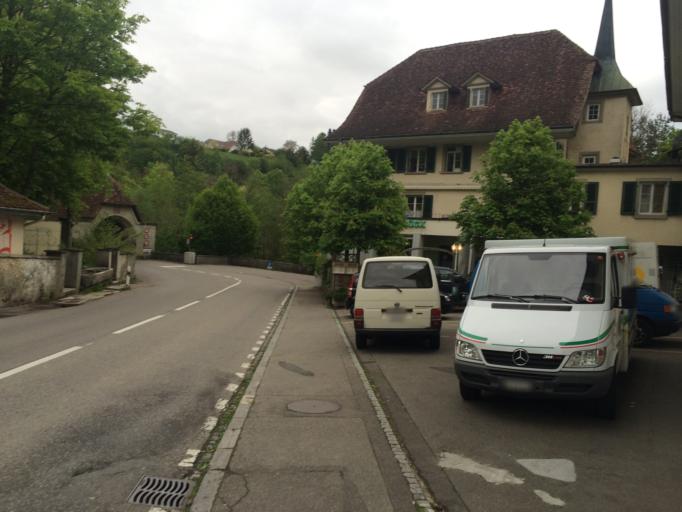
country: CH
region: Bern
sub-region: Bern-Mittelland District
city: Kirchlindach
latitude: 46.9730
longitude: 7.4278
